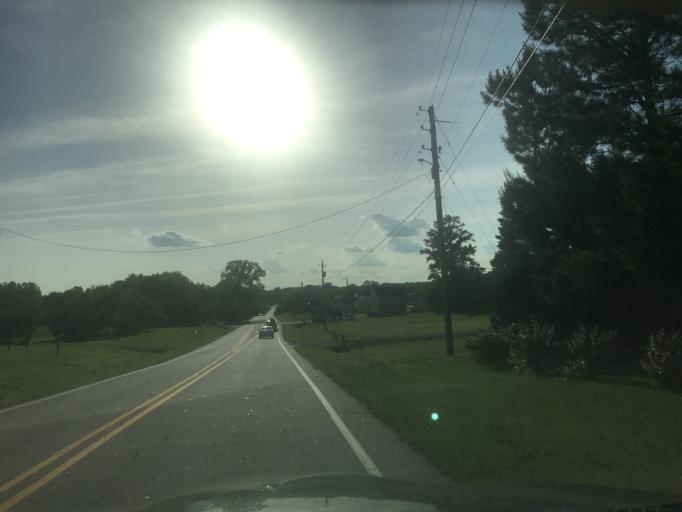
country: US
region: North Carolina
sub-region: Wake County
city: Knightdale
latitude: 35.7479
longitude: -78.4573
